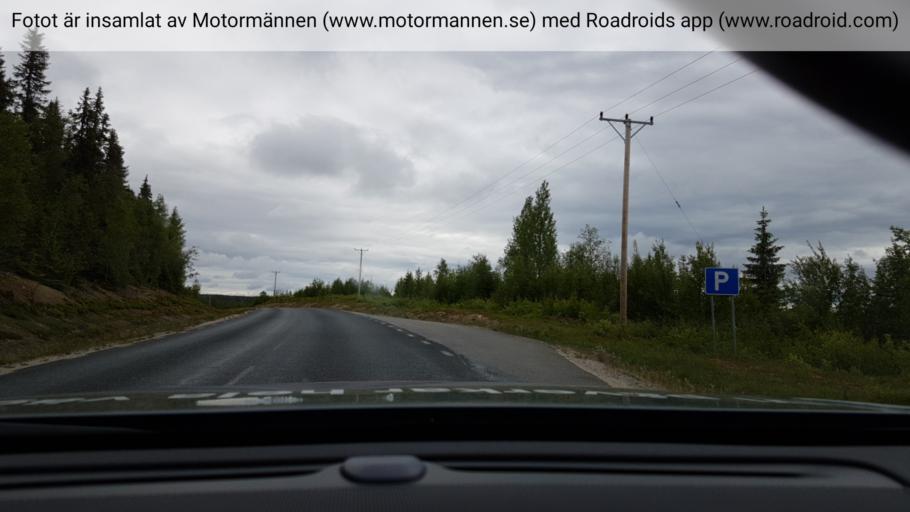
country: SE
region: Vaesterbotten
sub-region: Lycksele Kommun
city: Soderfors
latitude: 64.3834
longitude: 17.9958
